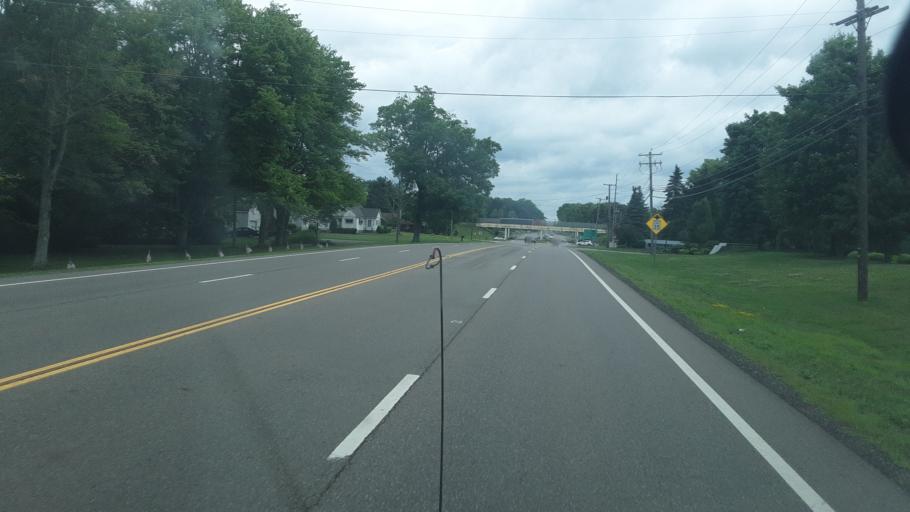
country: US
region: Ohio
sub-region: Trumbull County
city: Churchill
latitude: 41.2273
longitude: -80.6638
